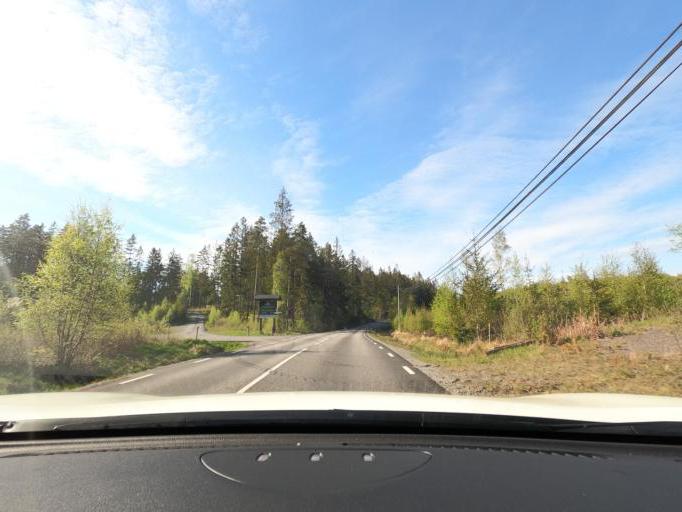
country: SE
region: Vaestra Goetaland
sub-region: Harryda Kommun
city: Landvetter
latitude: 57.6207
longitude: 12.2783
